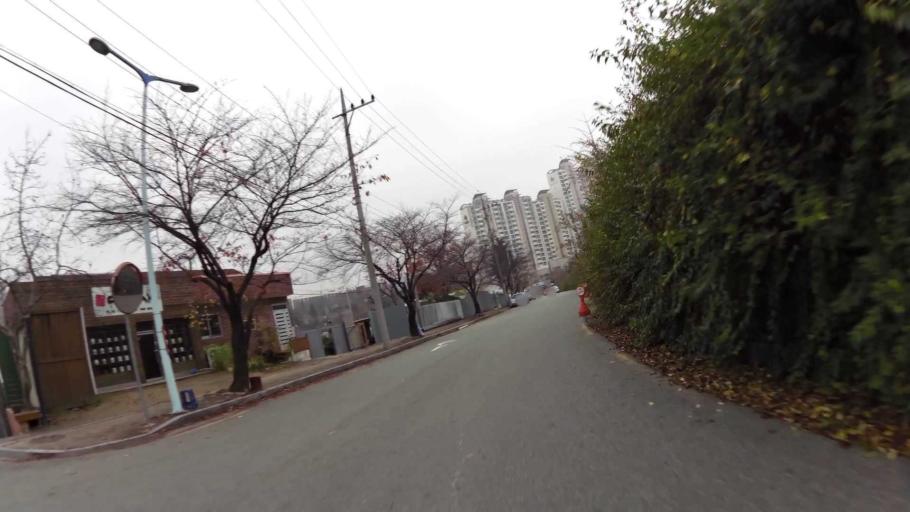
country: KR
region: Daegu
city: Daegu
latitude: 35.8553
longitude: 128.6582
